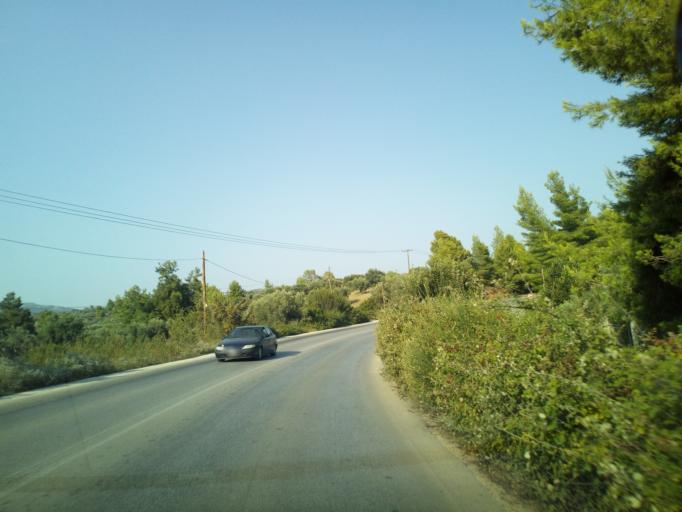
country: GR
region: Central Macedonia
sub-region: Nomos Chalkidikis
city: Nikiti
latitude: 40.2313
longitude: 23.6113
